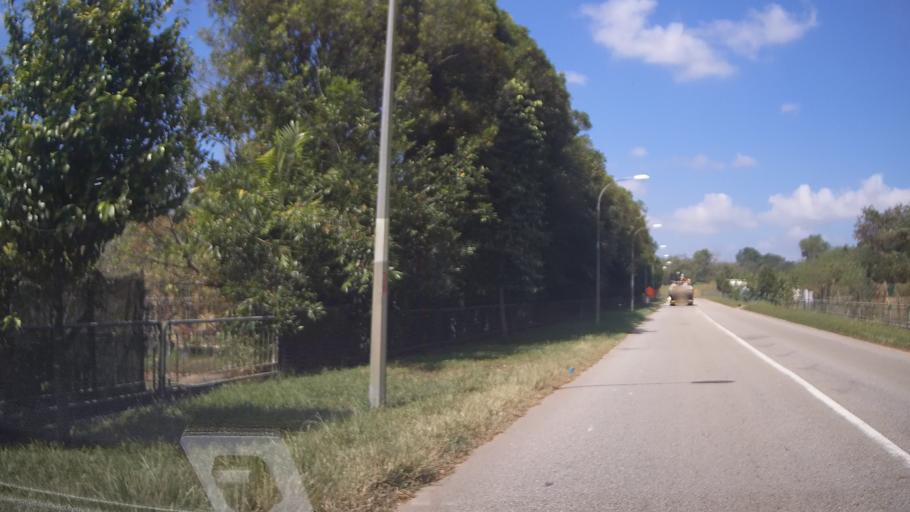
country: MY
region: Johor
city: Johor Bahru
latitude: 1.4334
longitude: 103.7138
